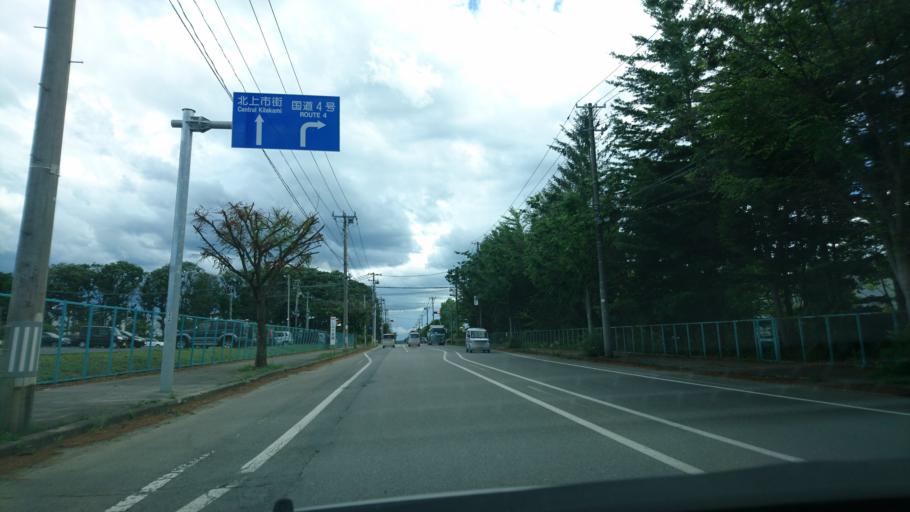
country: JP
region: Iwate
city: Hanamaki
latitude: 39.3358
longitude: 141.1284
